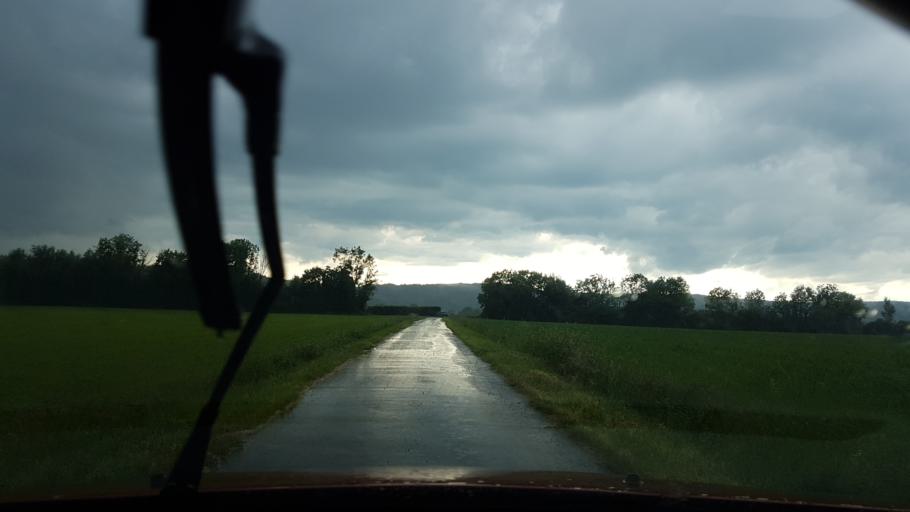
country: FR
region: Franche-Comte
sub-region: Departement du Jura
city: Clairvaux-les-Lacs
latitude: 46.5533
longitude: 5.7130
